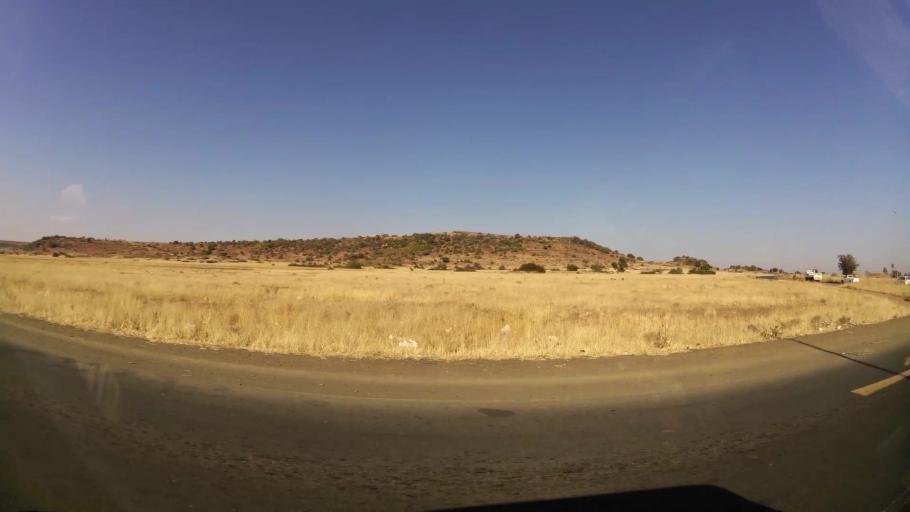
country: ZA
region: Orange Free State
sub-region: Mangaung Metropolitan Municipality
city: Bloemfontein
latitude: -29.1724
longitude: 26.2004
